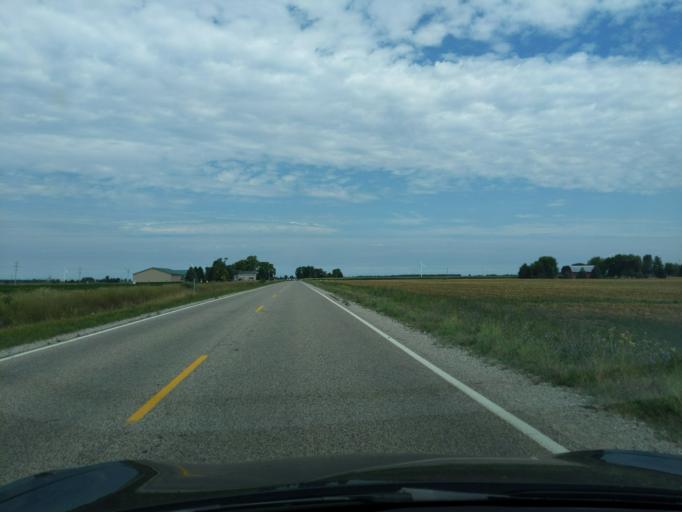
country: US
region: Michigan
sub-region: Gratiot County
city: Breckenridge
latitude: 43.3609
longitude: -84.4298
